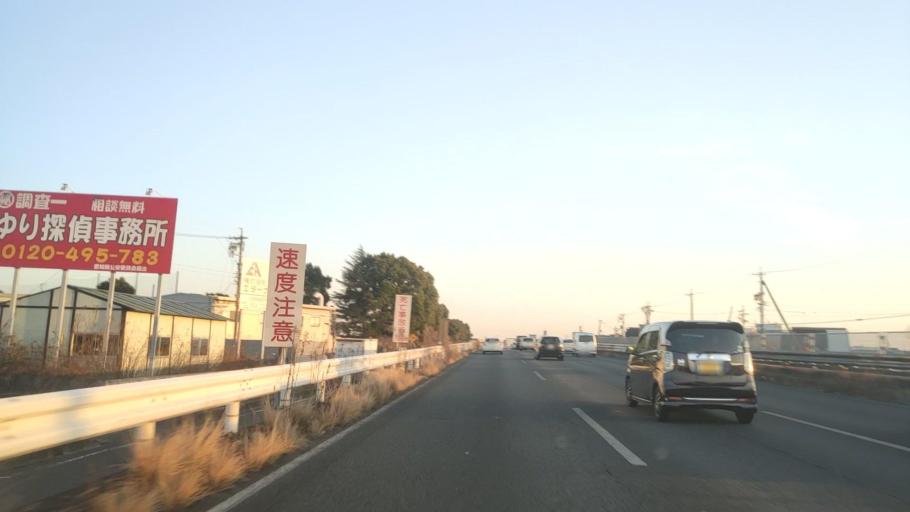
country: JP
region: Aichi
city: Kuroda
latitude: 35.3323
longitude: 136.8029
